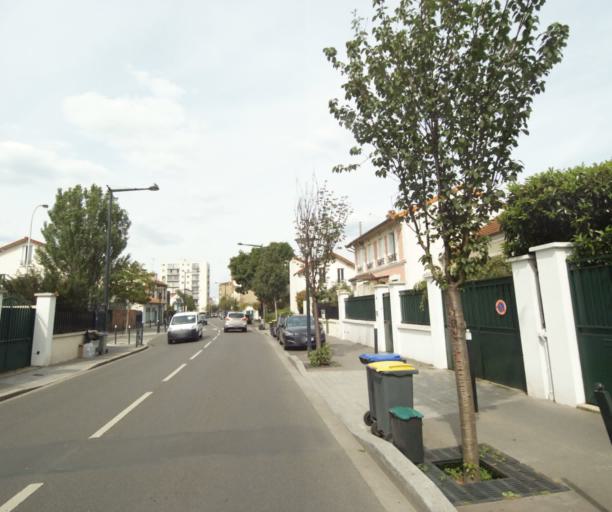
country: FR
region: Ile-de-France
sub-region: Departement des Hauts-de-Seine
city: Bois-Colombes
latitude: 48.9197
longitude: 2.2767
